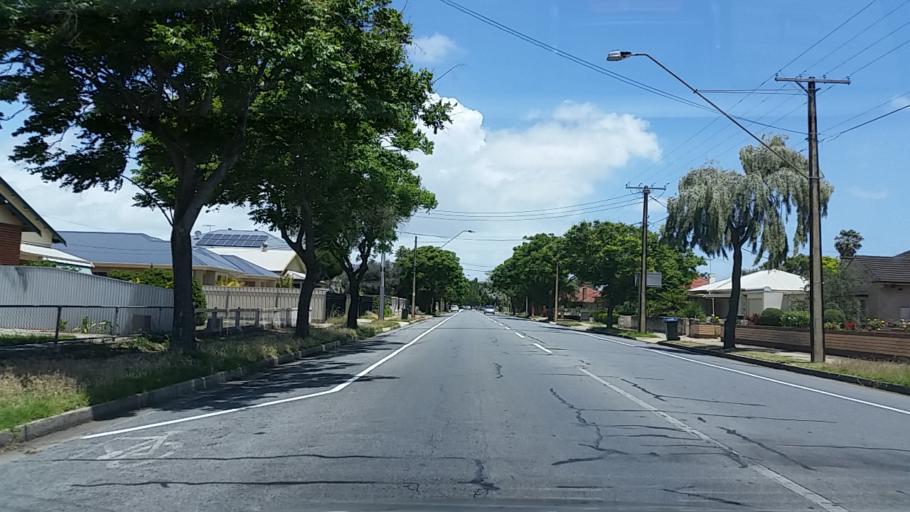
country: AU
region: South Australia
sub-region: Charles Sturt
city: Woodville
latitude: -34.8848
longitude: 138.5632
